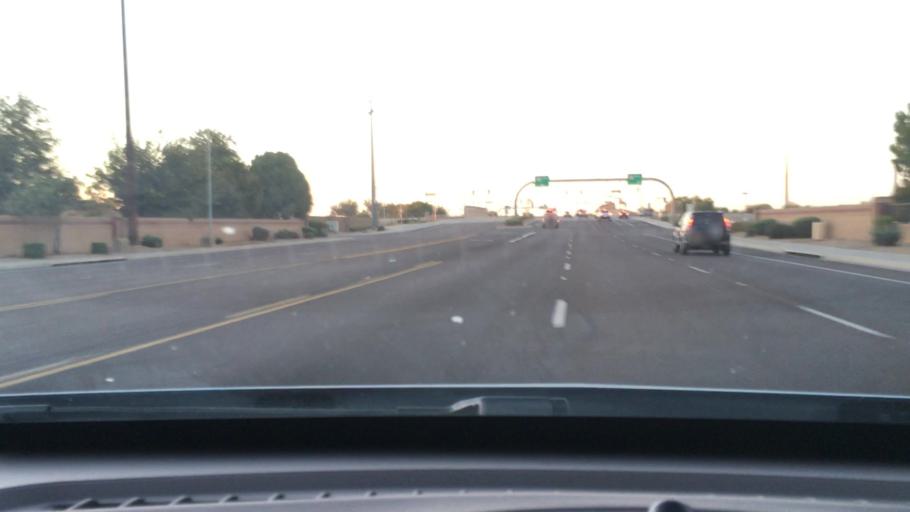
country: US
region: Arizona
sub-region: Maricopa County
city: Chandler
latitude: 33.2851
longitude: -111.8243
